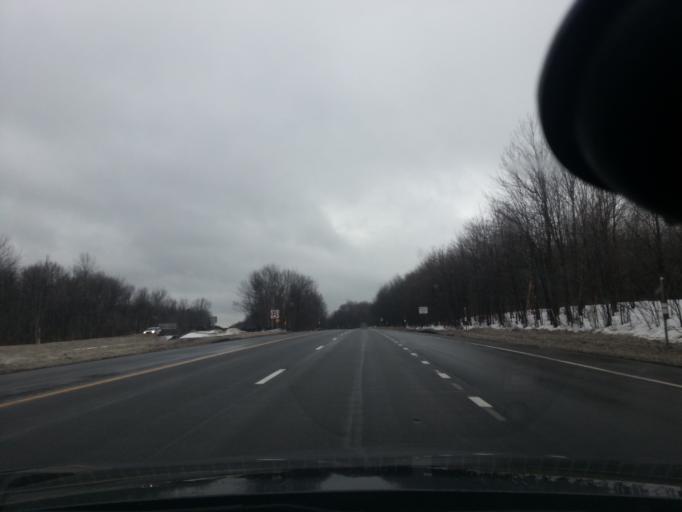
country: US
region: New York
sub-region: Oswego County
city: Central Square
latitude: 43.4022
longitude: -76.1179
